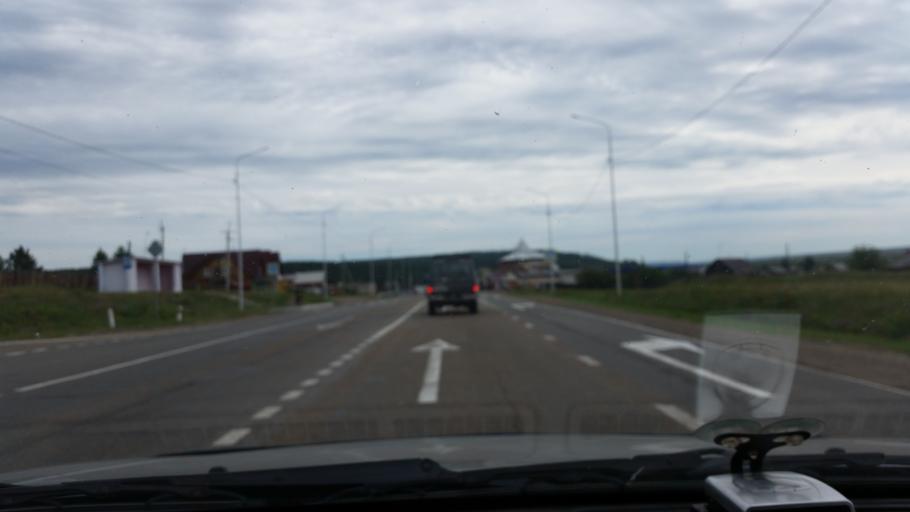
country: RU
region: Irkutsk
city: Oyek
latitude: 52.6543
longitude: 104.5358
